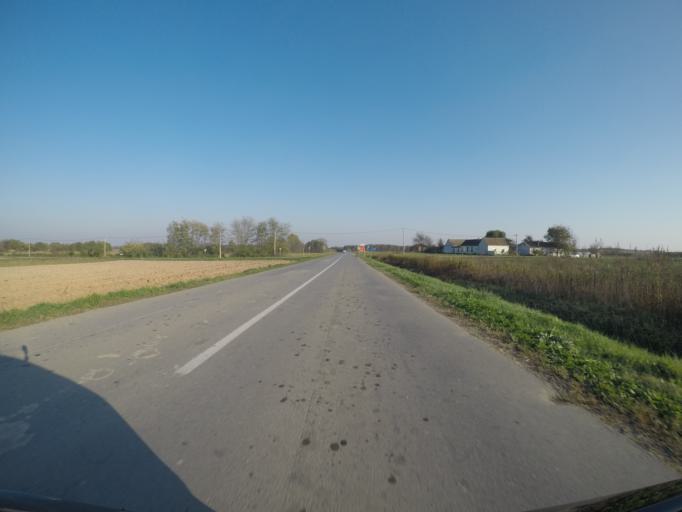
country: HR
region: Virovitick-Podravska
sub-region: Grad Virovitica
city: Virovitica
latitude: 45.8836
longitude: 17.3872
